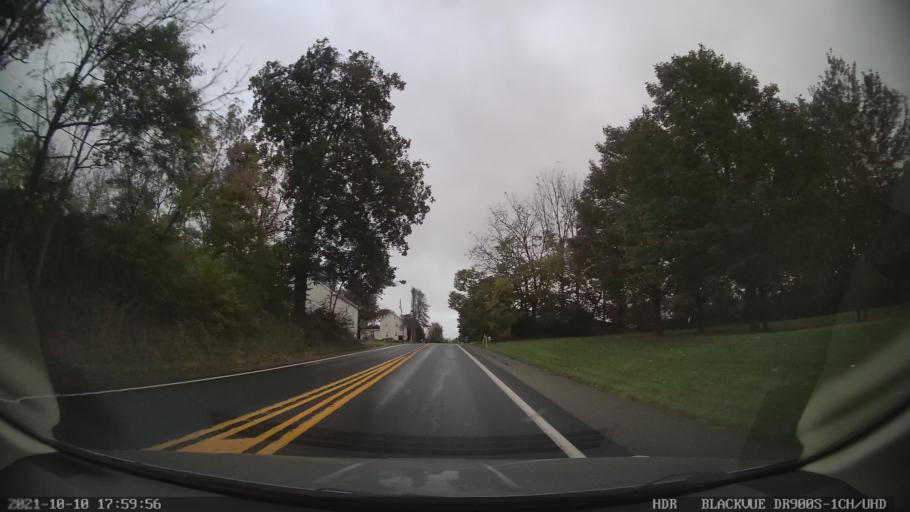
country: US
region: Pennsylvania
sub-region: Lehigh County
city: Egypt
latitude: 40.6420
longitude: -75.5531
